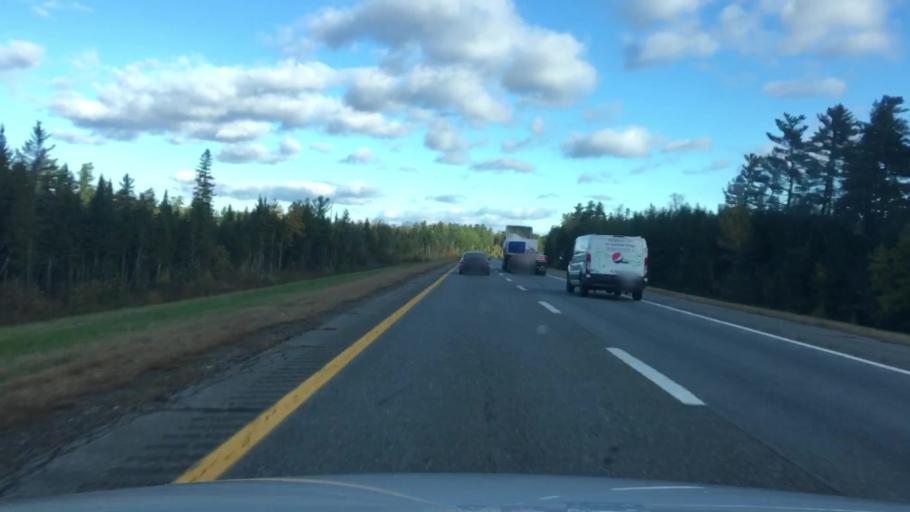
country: US
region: Maine
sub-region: Penobscot County
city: Greenbush
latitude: 45.1467
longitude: -68.7026
